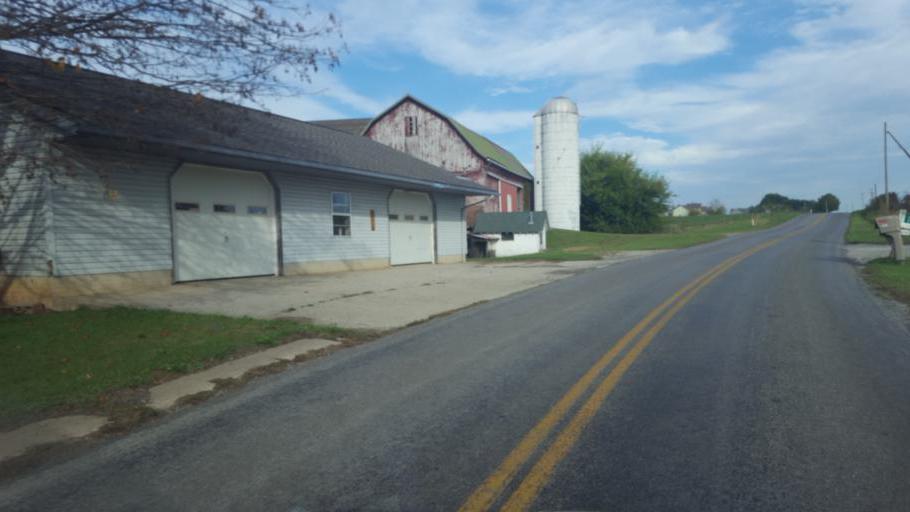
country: US
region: Ohio
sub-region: Holmes County
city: Millersburg
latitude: 40.5741
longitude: -81.8334
